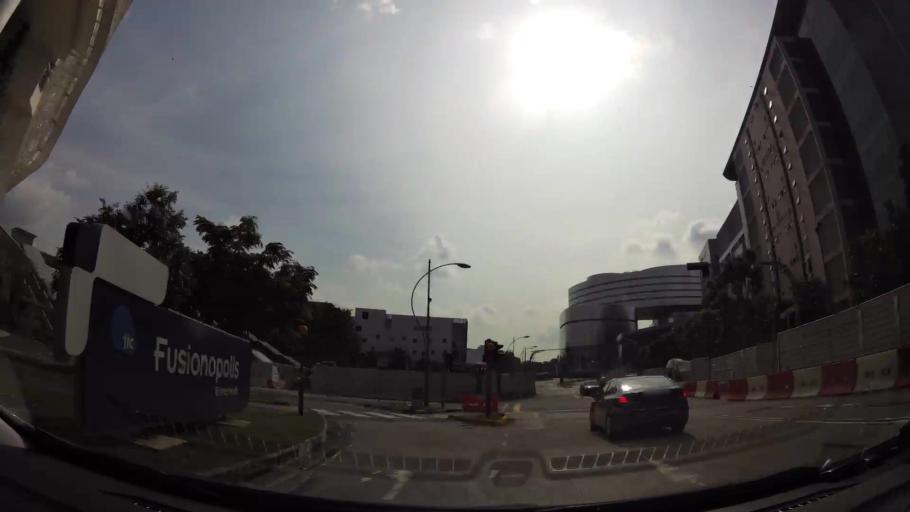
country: SG
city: Singapore
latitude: 1.2974
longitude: 103.7901
